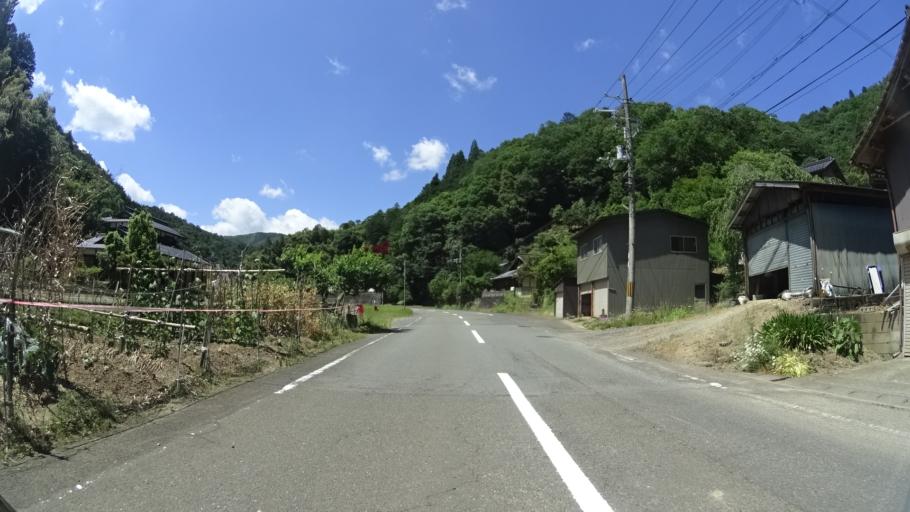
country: JP
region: Kyoto
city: Miyazu
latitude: 35.4138
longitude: 135.1884
